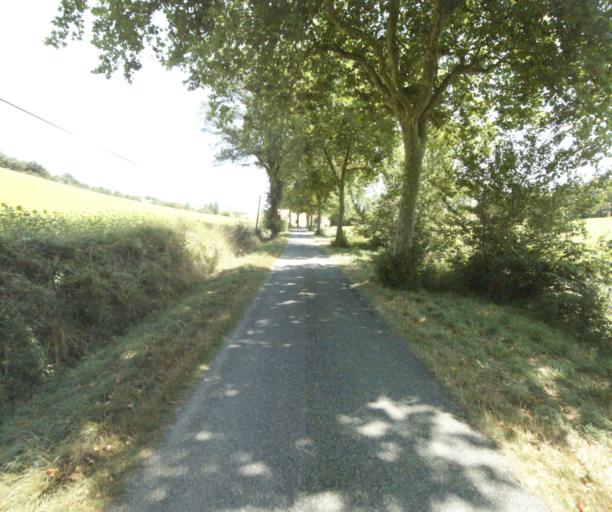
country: FR
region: Midi-Pyrenees
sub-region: Departement de la Haute-Garonne
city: Saint-Felix-Lauragais
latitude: 43.4448
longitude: 1.8543
